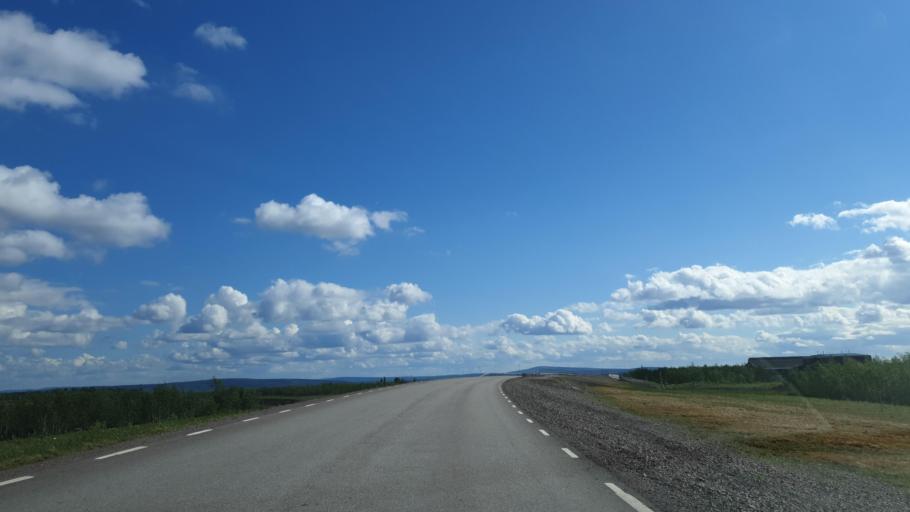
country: SE
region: Norrbotten
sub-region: Kiruna Kommun
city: Kiruna
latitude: 67.7974
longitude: 20.2339
